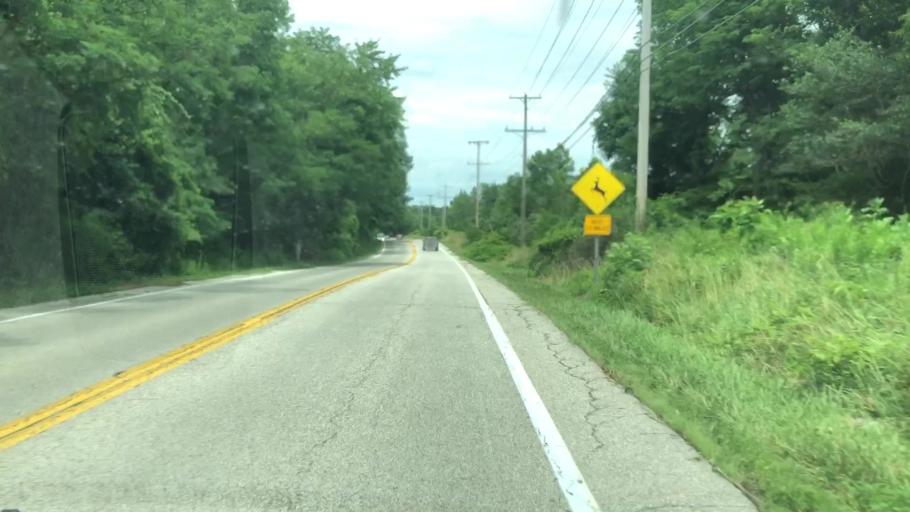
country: US
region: Ohio
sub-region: Summit County
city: Fairlawn
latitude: 41.1719
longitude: -81.5613
